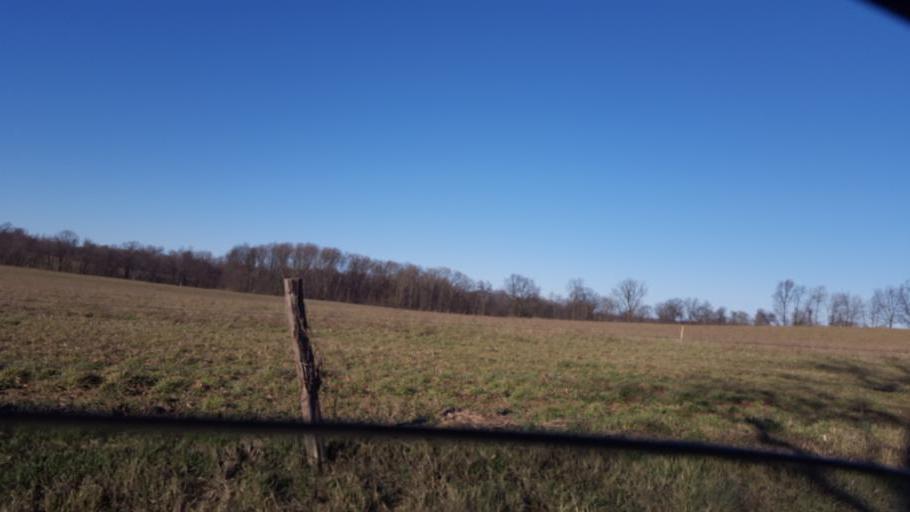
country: US
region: Ohio
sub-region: Holmes County
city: Millersburg
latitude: 40.5986
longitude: -81.7731
